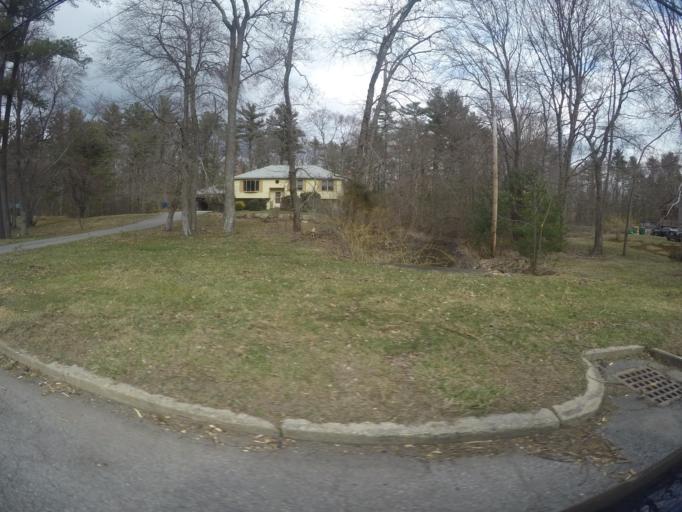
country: US
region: Massachusetts
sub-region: Bristol County
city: Easton
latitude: 42.0410
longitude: -71.1140
